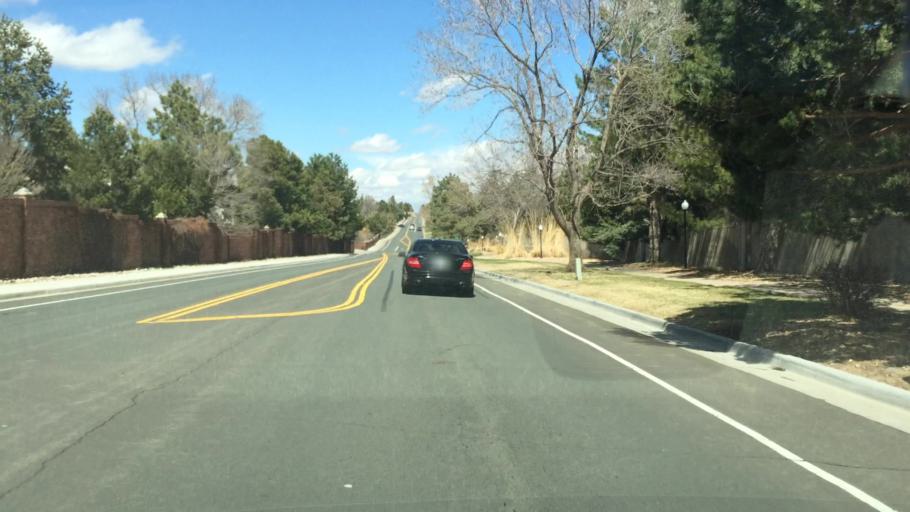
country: US
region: Colorado
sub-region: Arapahoe County
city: Centennial
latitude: 39.6059
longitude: -104.8761
